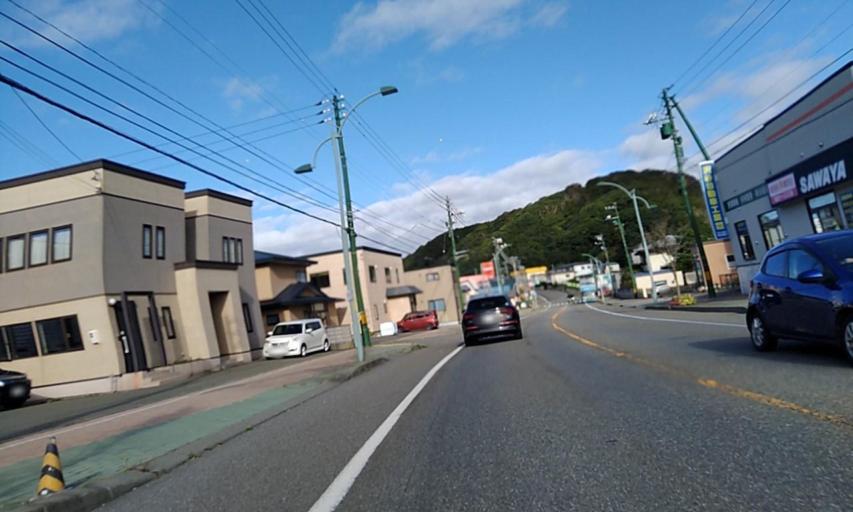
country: JP
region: Hokkaido
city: Shizunai-furukawacho
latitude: 42.2491
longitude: 142.5542
